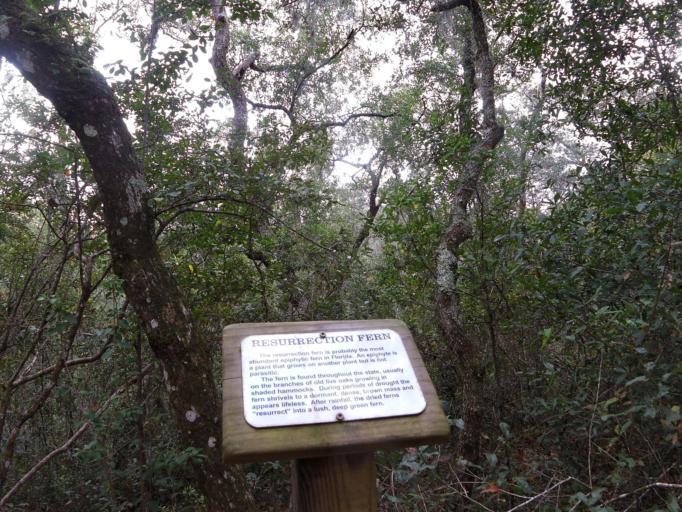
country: US
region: Florida
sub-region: Clay County
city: Keystone Heights
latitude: 29.8361
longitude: -81.9501
